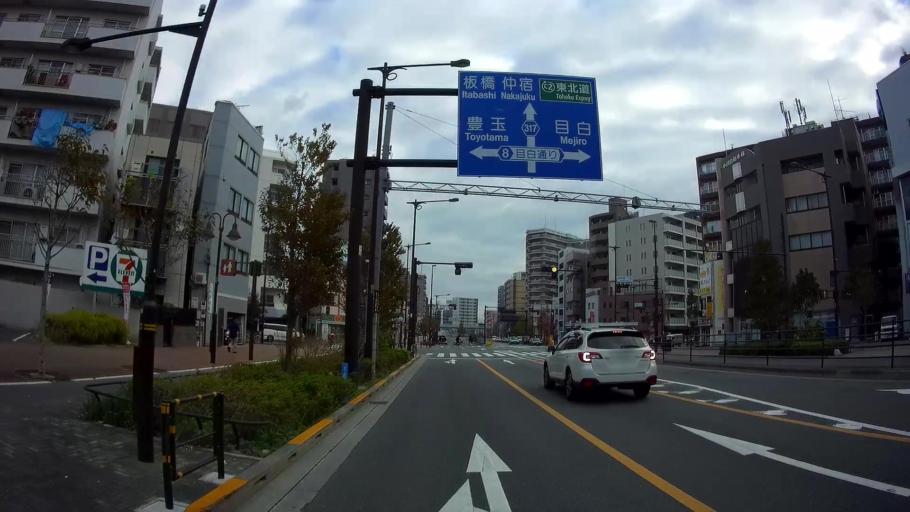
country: JP
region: Tokyo
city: Tokyo
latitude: 35.7221
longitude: 139.6921
